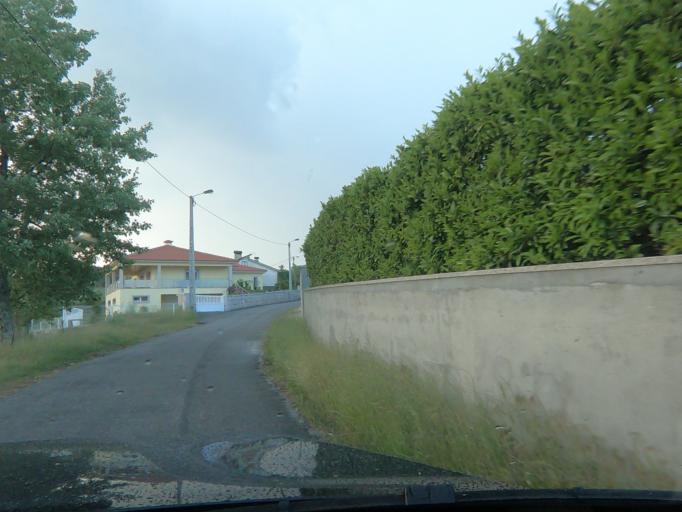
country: PT
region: Vila Real
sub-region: Vila Real
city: Vila Real
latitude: 41.3165
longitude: -7.6830
